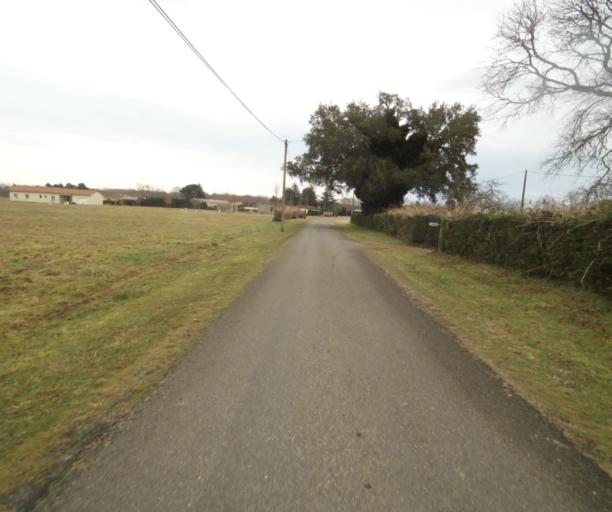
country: FR
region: Aquitaine
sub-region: Departement des Landes
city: Gabarret
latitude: 44.0122
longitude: -0.0272
